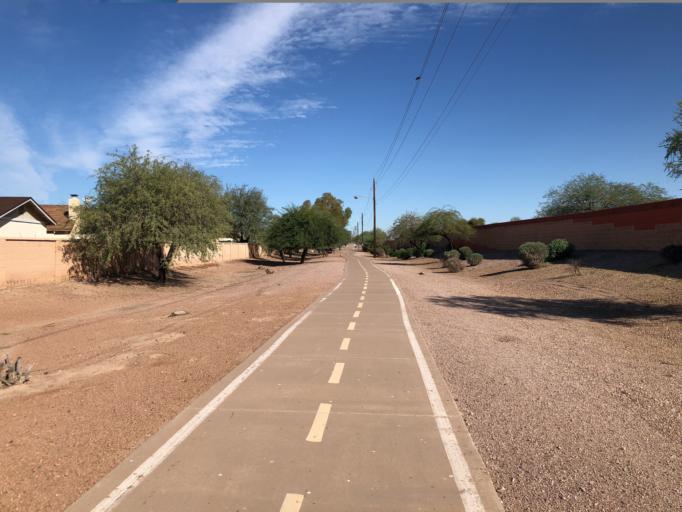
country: US
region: Arizona
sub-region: Maricopa County
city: Tempe
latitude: 33.4569
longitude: -111.8921
